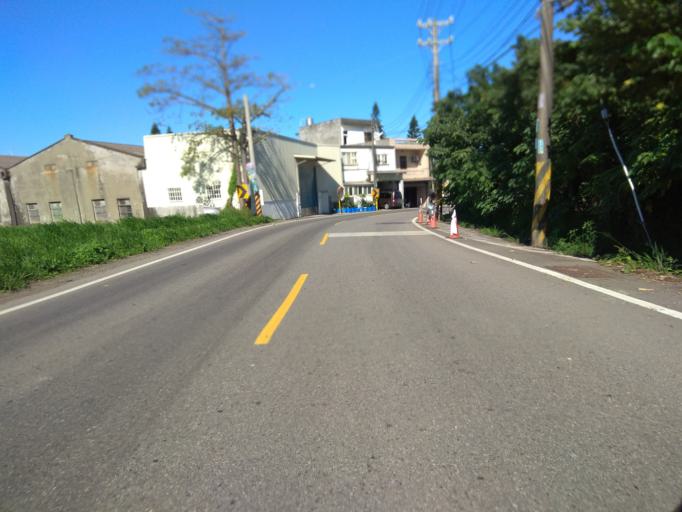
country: TW
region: Taiwan
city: Taoyuan City
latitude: 24.9901
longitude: 121.1325
